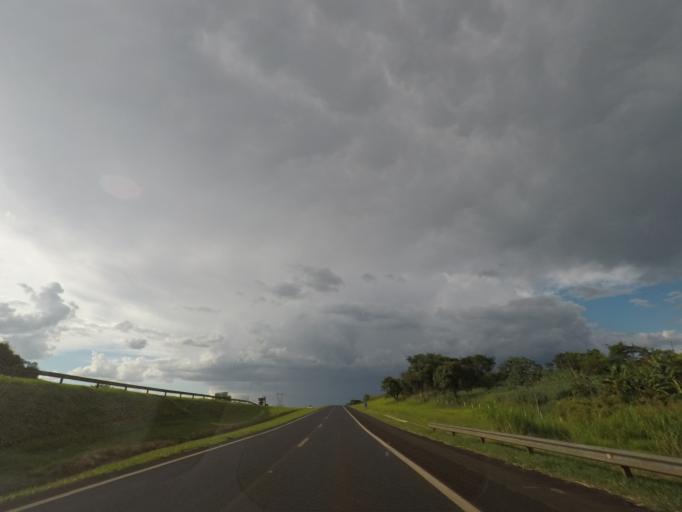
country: BR
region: Sao Paulo
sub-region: Jardinopolis
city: Jardinopolis
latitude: -21.0261
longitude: -47.8373
